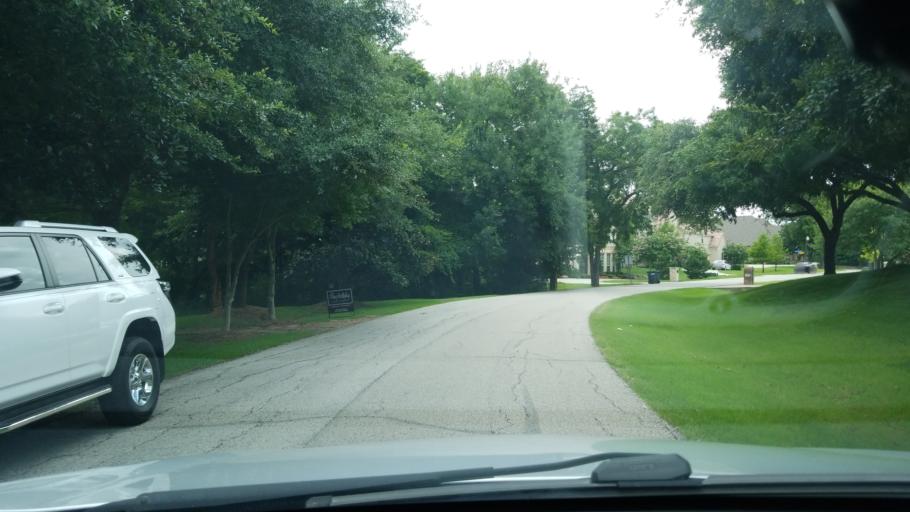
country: US
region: Texas
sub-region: Dallas County
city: Coppell
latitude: 32.9566
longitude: -96.9790
